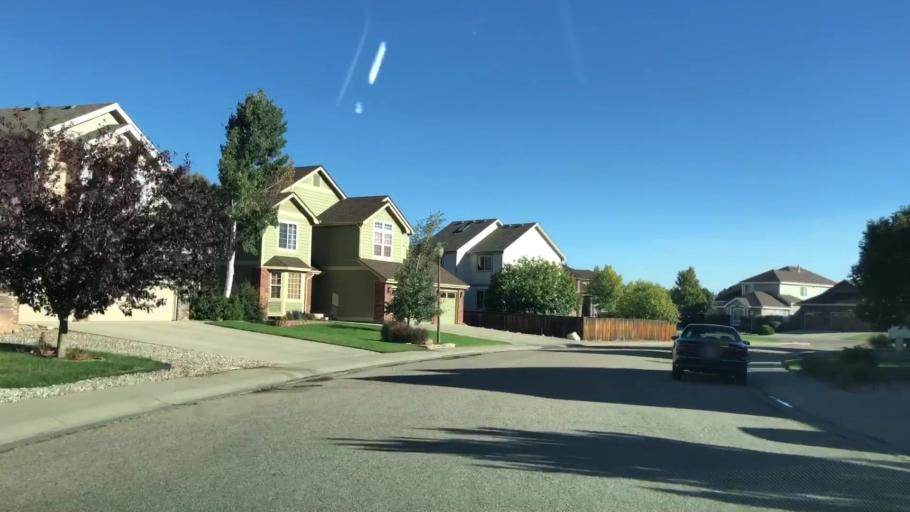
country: US
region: Colorado
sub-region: Larimer County
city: Loveland
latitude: 40.3994
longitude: -105.1374
